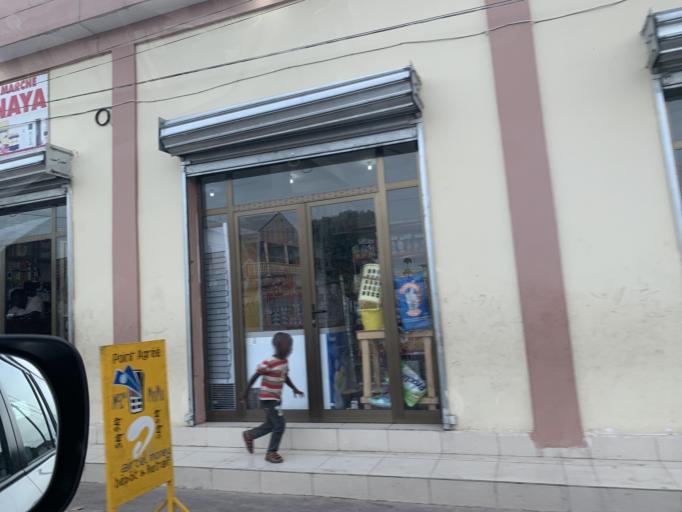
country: CG
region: Brazzaville
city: Brazzaville
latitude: -4.2561
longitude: 15.2886
